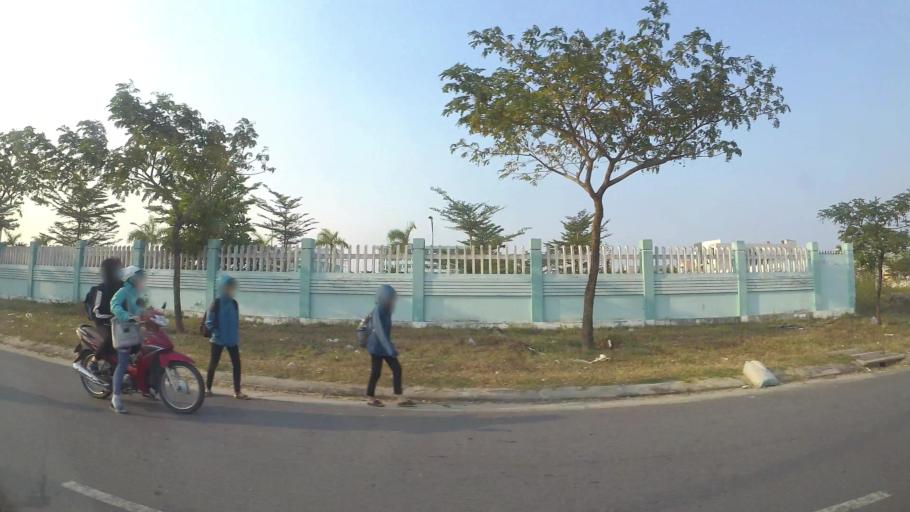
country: VN
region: Da Nang
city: Ngu Hanh Son
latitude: 15.9780
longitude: 108.2482
